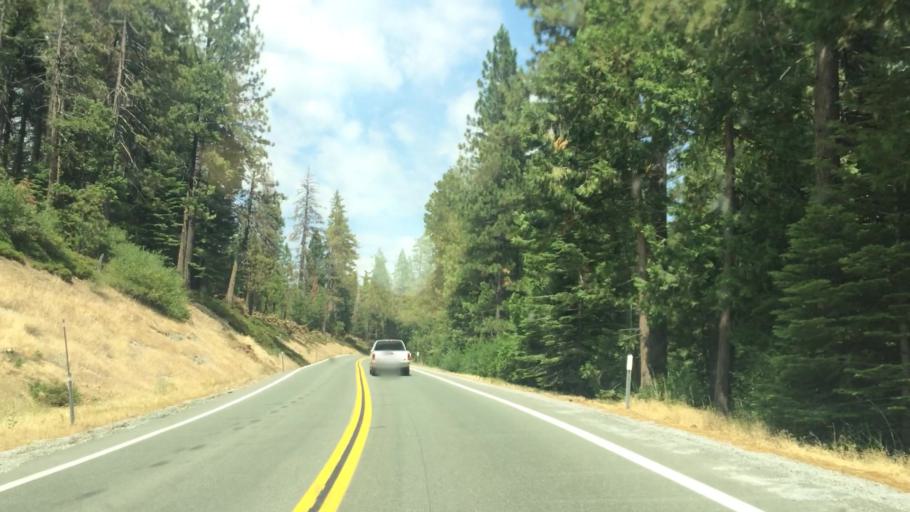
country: US
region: California
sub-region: Amador County
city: Pioneer
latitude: 38.5377
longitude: -120.3981
